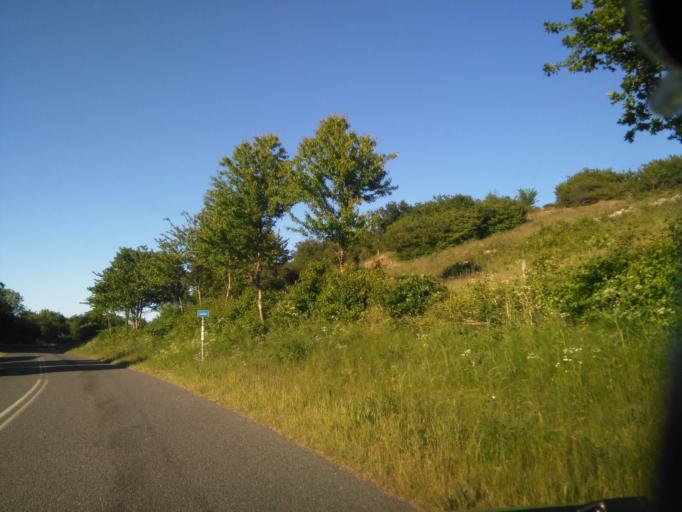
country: DK
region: Capital Region
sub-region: Bornholm Kommune
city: Ronne
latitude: 55.2826
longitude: 14.7693
